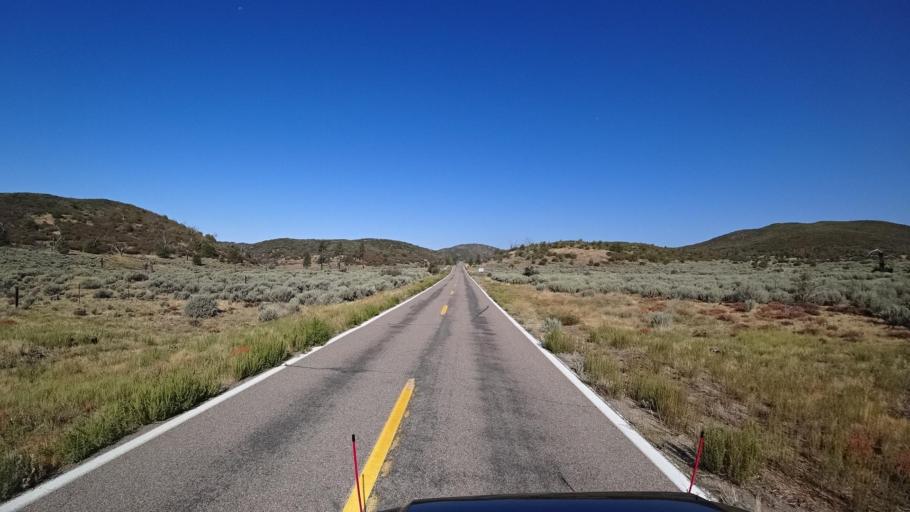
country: US
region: California
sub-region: San Diego County
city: Pine Valley
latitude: 32.9175
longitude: -116.4694
